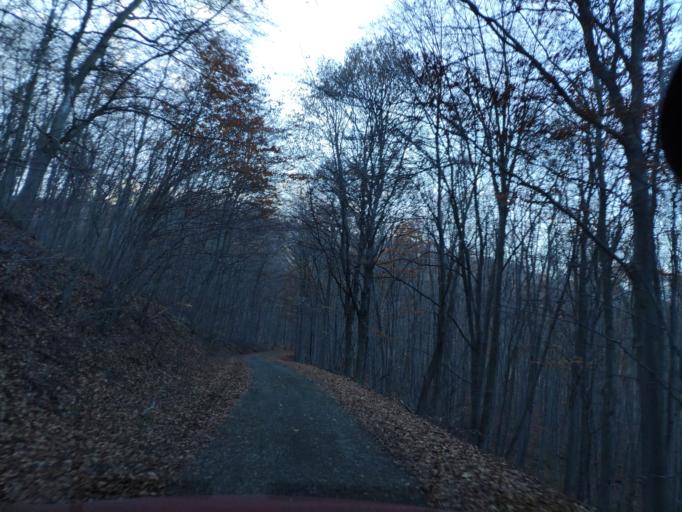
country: SK
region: Kosicky
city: Secovce
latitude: 48.5846
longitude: 21.5070
